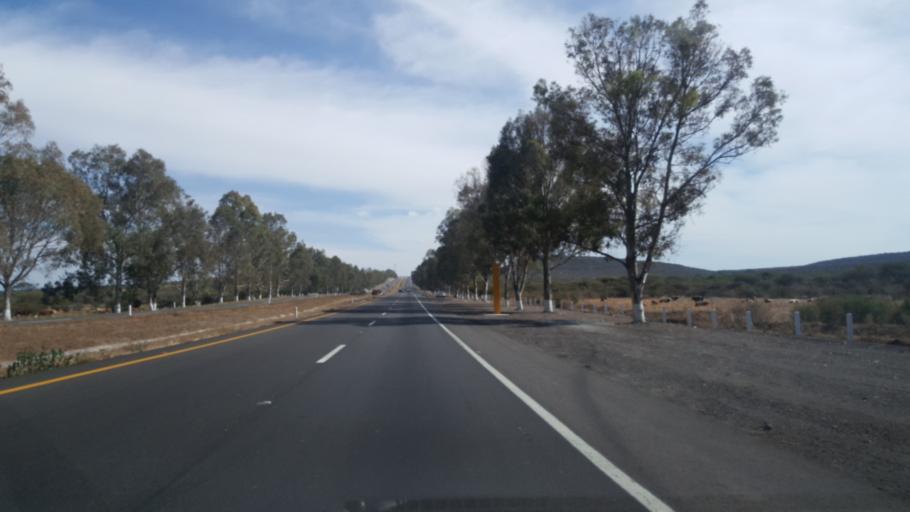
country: MX
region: Jalisco
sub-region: Lagos de Moreno
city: Cristeros [Fraccionamiento]
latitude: 21.2717
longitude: -101.9758
